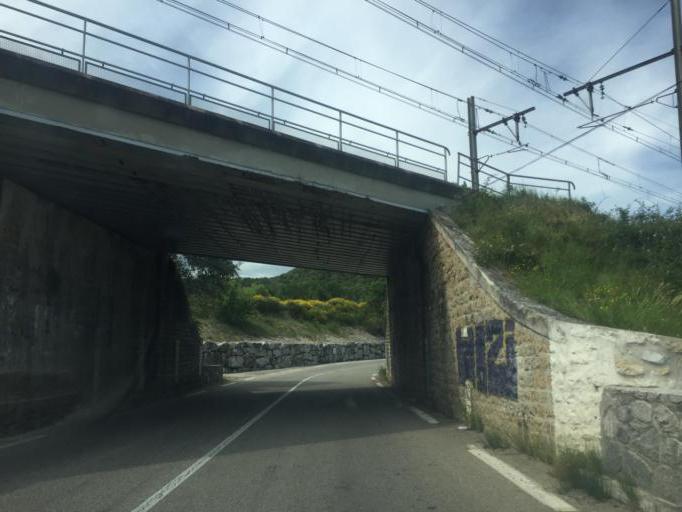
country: FR
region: Rhone-Alpes
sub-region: Departement de l'Ardeche
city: Bourg-Saint-Andeol
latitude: 44.4034
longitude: 4.6461
